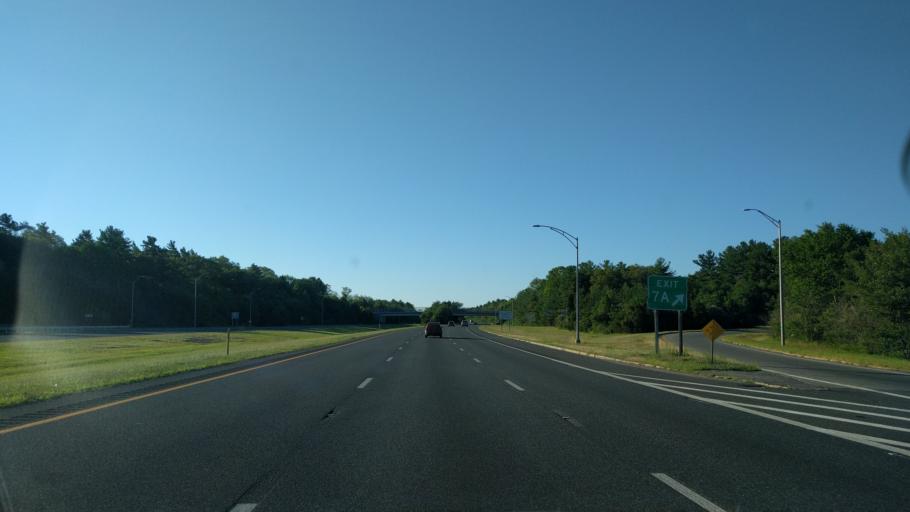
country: US
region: Massachusetts
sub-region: Bristol County
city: Raynham Center
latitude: 41.9446
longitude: -71.0192
